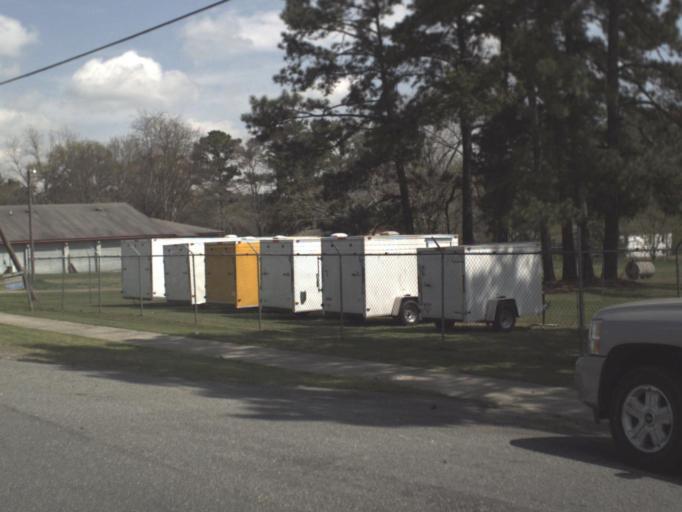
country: US
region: Florida
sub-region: Gadsden County
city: Havana
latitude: 30.6370
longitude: -84.4174
